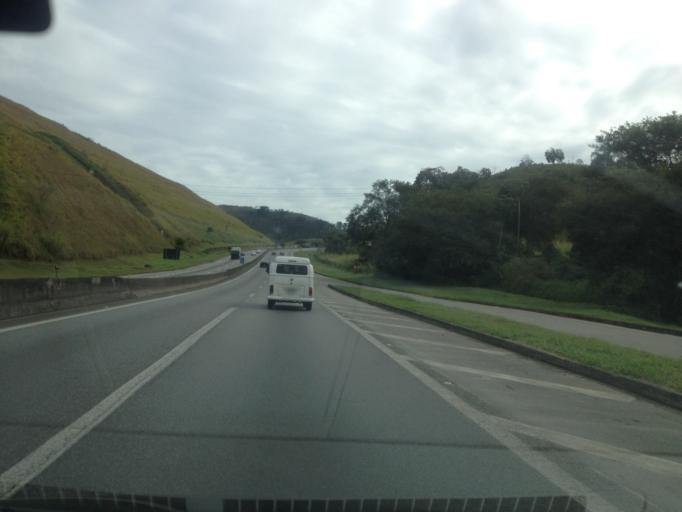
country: BR
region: Rio de Janeiro
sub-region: Pirai
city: Pirai
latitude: -22.6209
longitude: -43.9252
